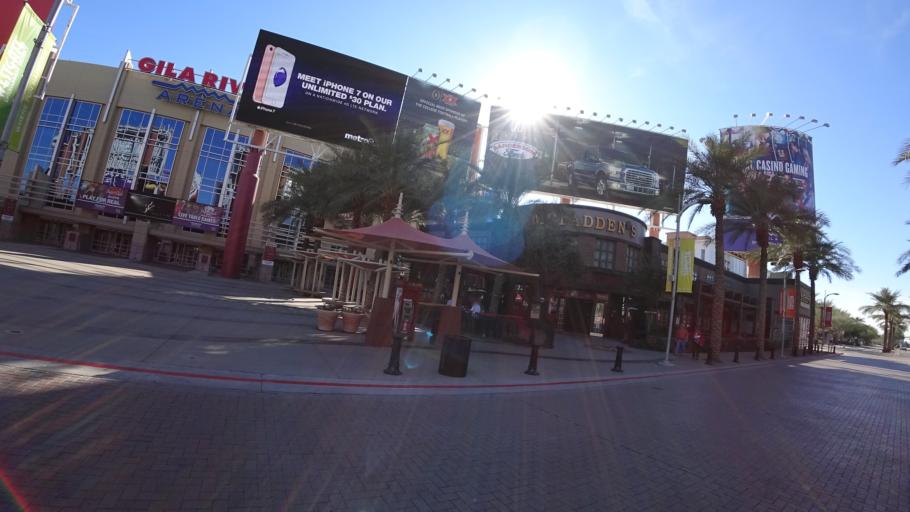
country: US
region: Arizona
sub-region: Maricopa County
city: Peoria
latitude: 33.5331
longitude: -112.2614
